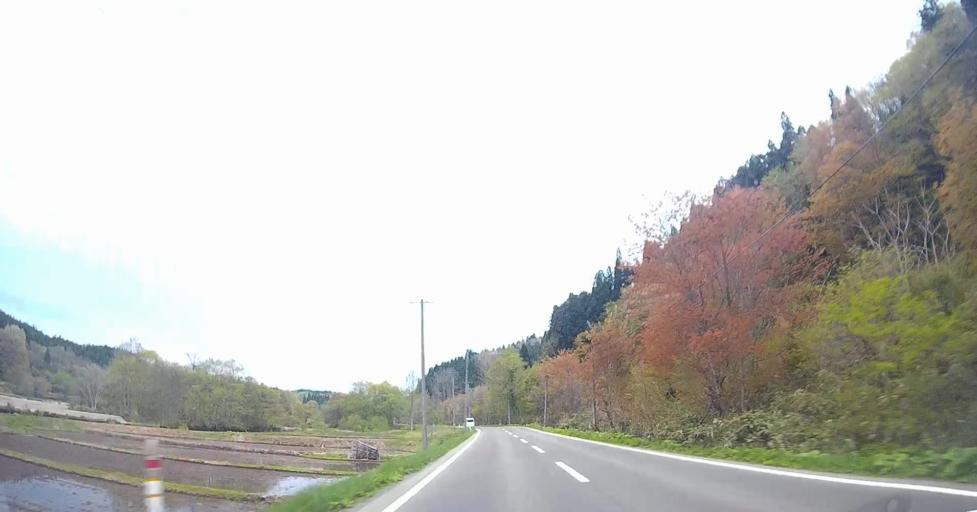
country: JP
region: Aomori
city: Goshogawara
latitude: 41.1248
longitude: 140.5198
